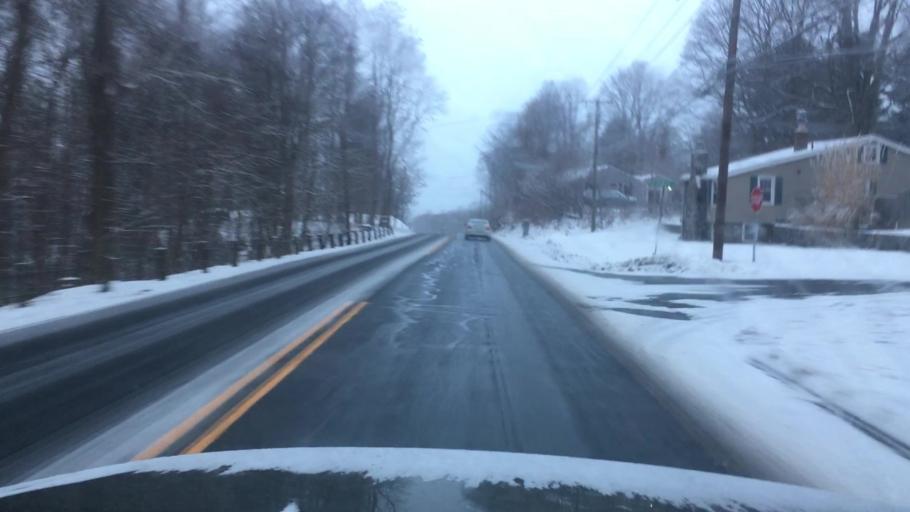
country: US
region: Connecticut
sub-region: Tolland County
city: Somers
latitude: 41.9832
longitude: -72.4208
